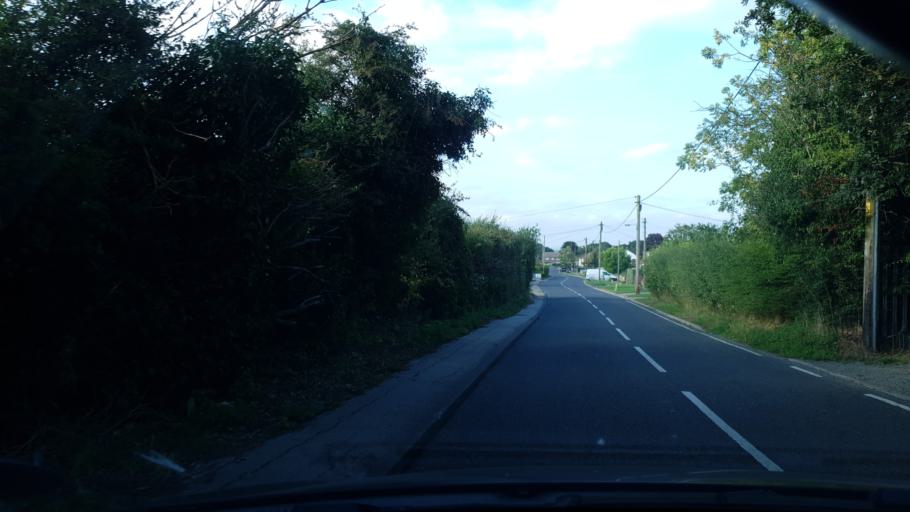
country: GB
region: England
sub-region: Essex
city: Frinton-on-Sea
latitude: 51.8491
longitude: 1.2239
